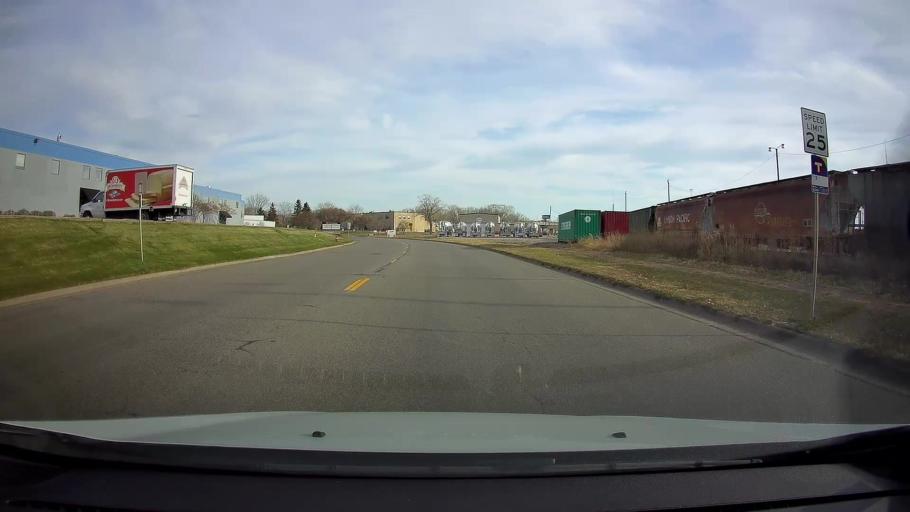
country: US
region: Minnesota
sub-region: Ramsey County
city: Lauderdale
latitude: 44.9778
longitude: -93.2098
